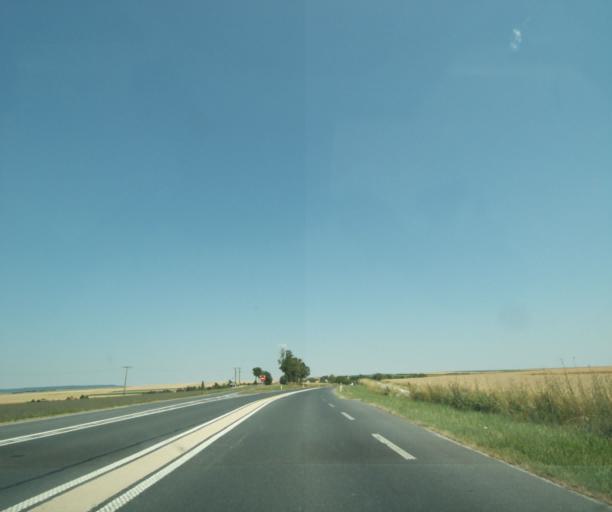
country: FR
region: Champagne-Ardenne
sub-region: Departement de la Marne
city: Fagnieres
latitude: 49.0591
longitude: 4.2979
